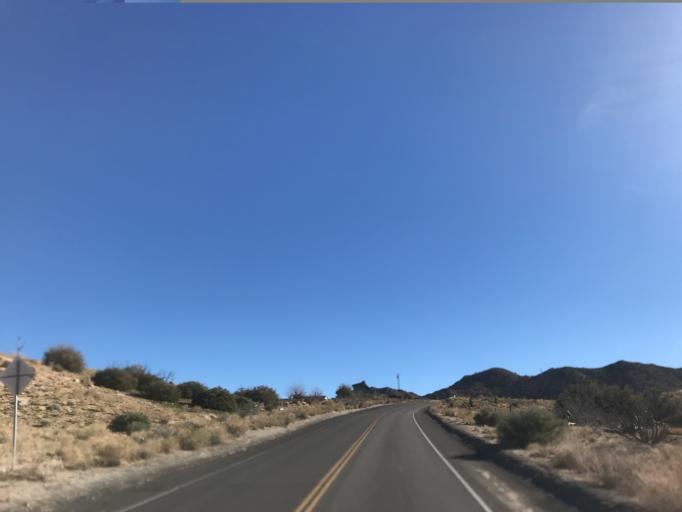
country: US
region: California
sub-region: San Bernardino County
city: Yucca Valley
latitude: 34.1600
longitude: -116.5022
